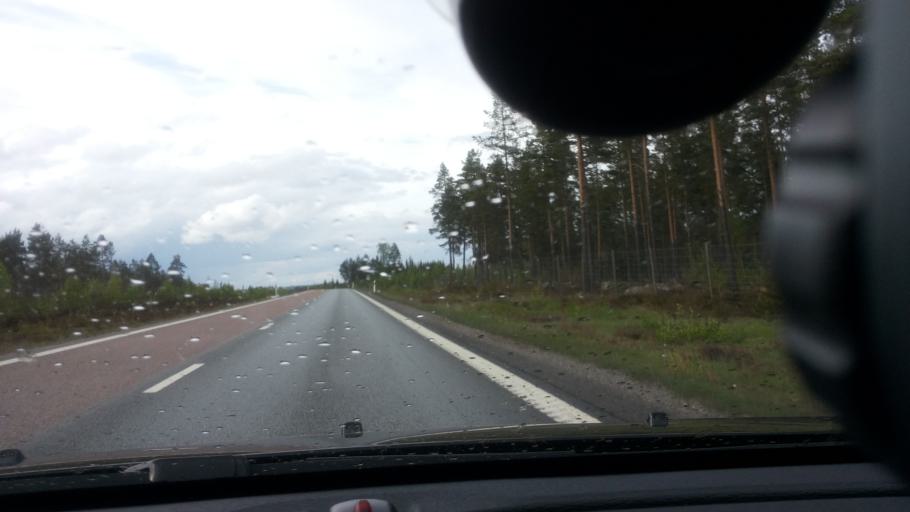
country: SE
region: Gaevleborg
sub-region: Soderhamns Kommun
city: Soderhamn
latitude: 61.3883
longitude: 16.9926
